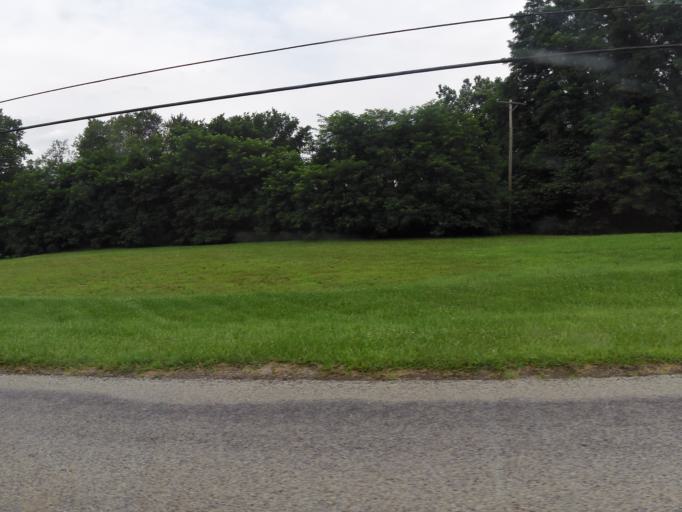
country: US
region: Ohio
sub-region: Warren County
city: Waynesville
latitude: 39.5237
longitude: -84.0738
